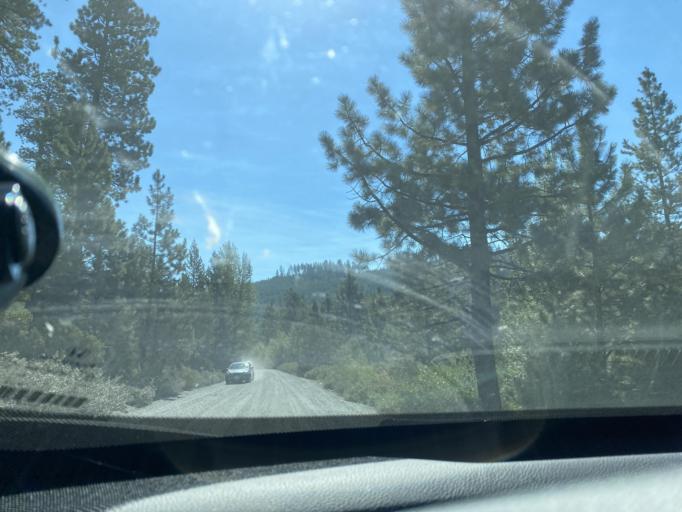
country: US
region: Oregon
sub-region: Deschutes County
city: Sunriver
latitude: 44.0311
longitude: -121.5624
